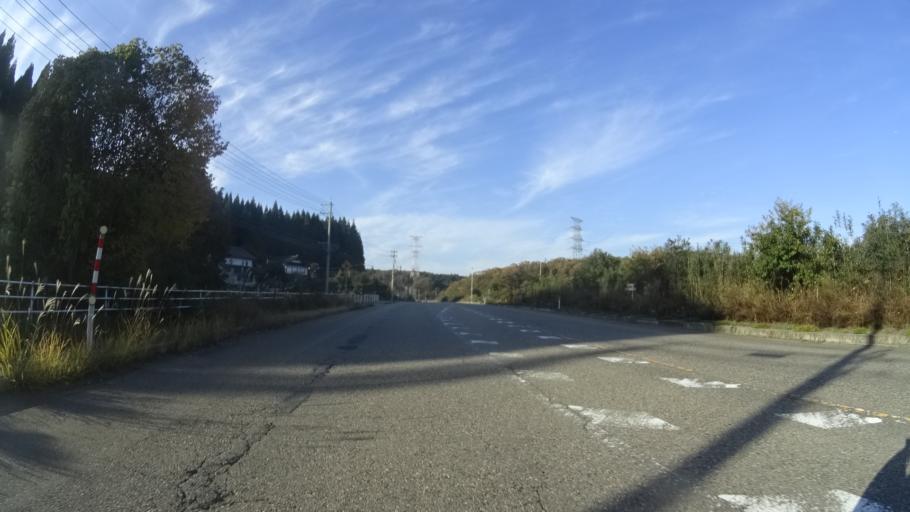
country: JP
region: Ishikawa
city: Hakui
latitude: 37.0435
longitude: 136.7764
